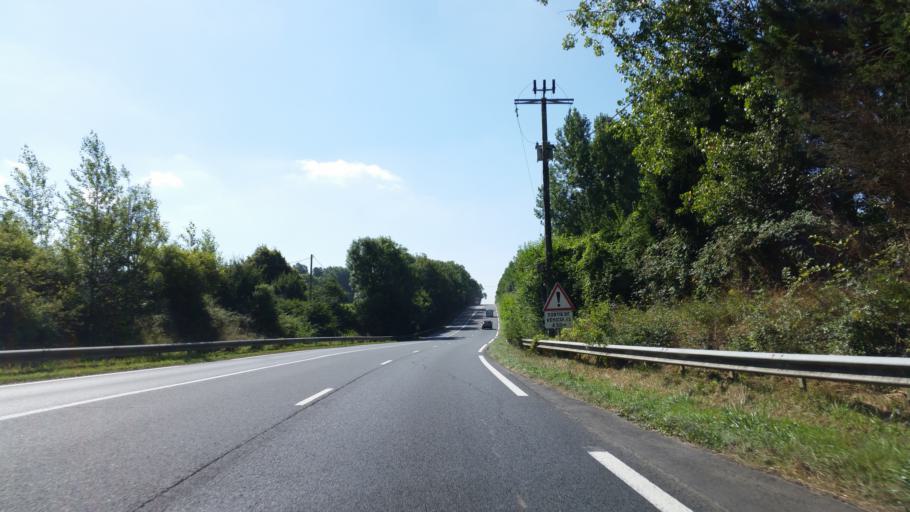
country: FR
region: Lower Normandy
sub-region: Departement du Calvados
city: Saint-Gatien-des-Bois
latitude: 49.2802
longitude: 0.2147
